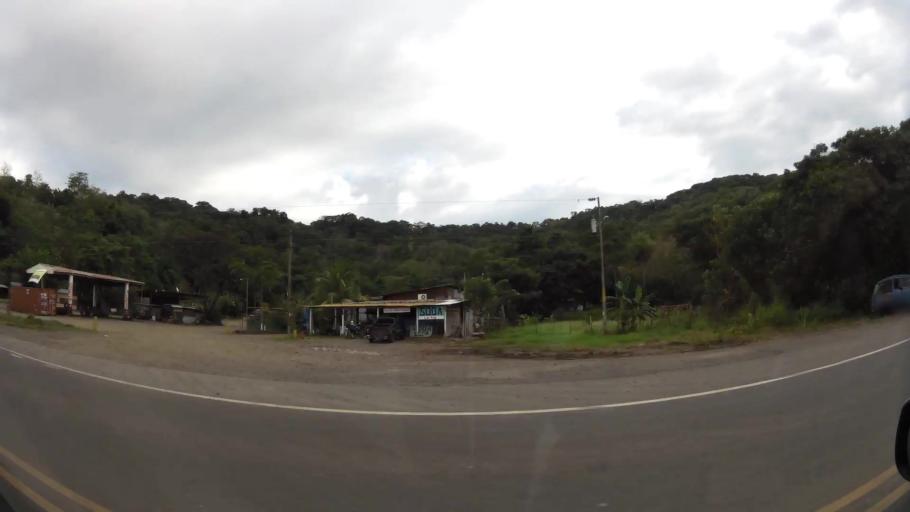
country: CR
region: Puntarenas
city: Esparza
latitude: 9.9175
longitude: -84.7010
